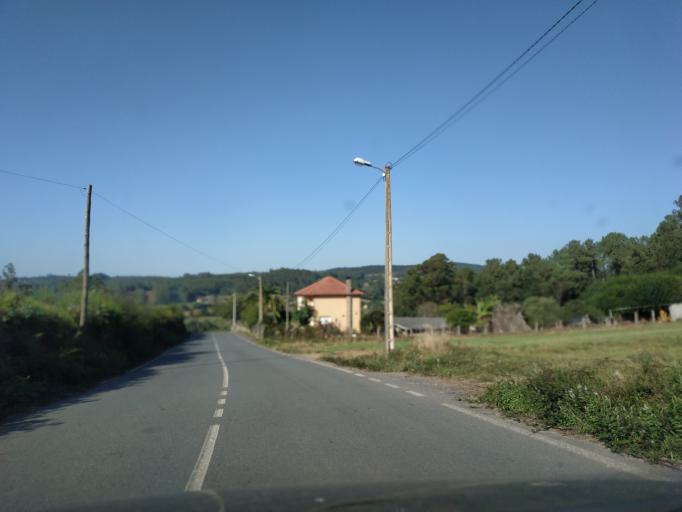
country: ES
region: Galicia
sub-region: Provincia da Coruna
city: Cerceda
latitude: 43.2283
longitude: -8.4926
